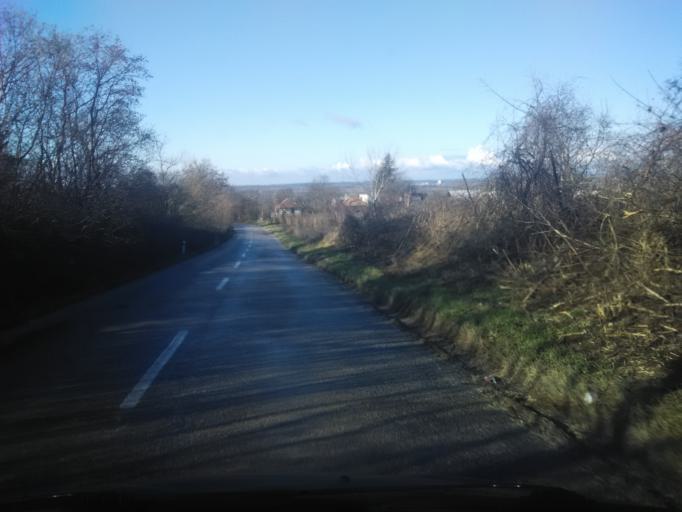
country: SK
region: Nitriansky
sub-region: Okres Nitra
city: Vrable
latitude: 48.2270
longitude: 18.2205
